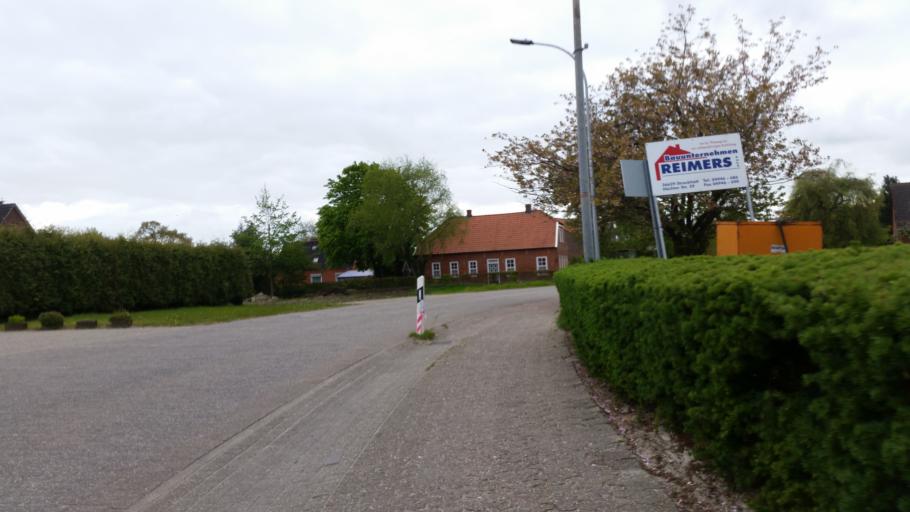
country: DE
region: Lower Saxony
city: Aurich
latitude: 53.4775
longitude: 7.4483
